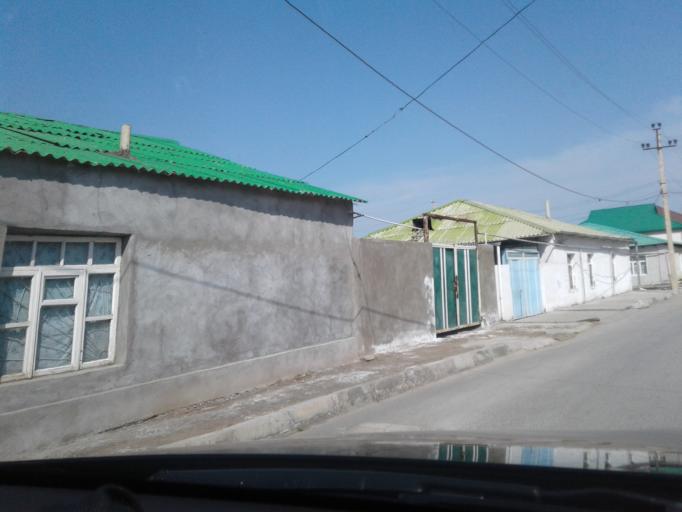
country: TM
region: Ahal
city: Ashgabat
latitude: 37.9861
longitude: 58.3957
